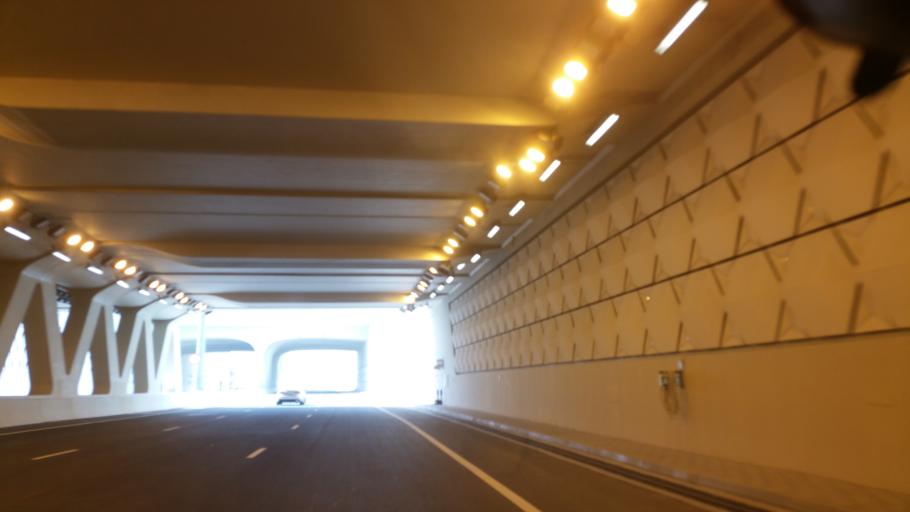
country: QA
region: Baladiyat Umm Salal
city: Umm Salal Muhammad
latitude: 25.4067
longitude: 51.5125
